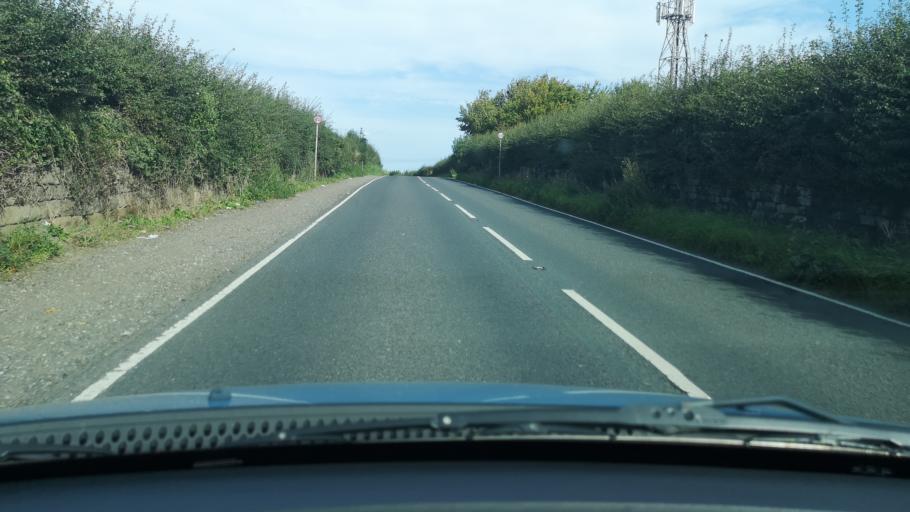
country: GB
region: England
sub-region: City and Borough of Wakefield
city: Walton
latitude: 53.6439
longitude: -1.4796
